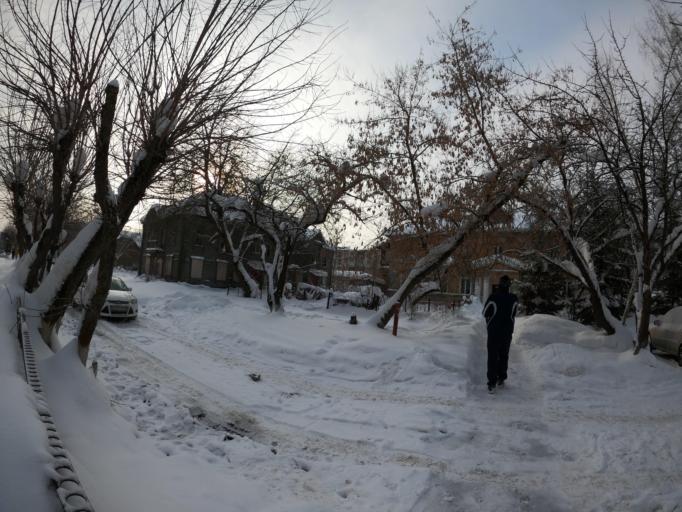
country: RU
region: Moskovskaya
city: Elektrogorsk
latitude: 55.8910
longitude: 38.7715
